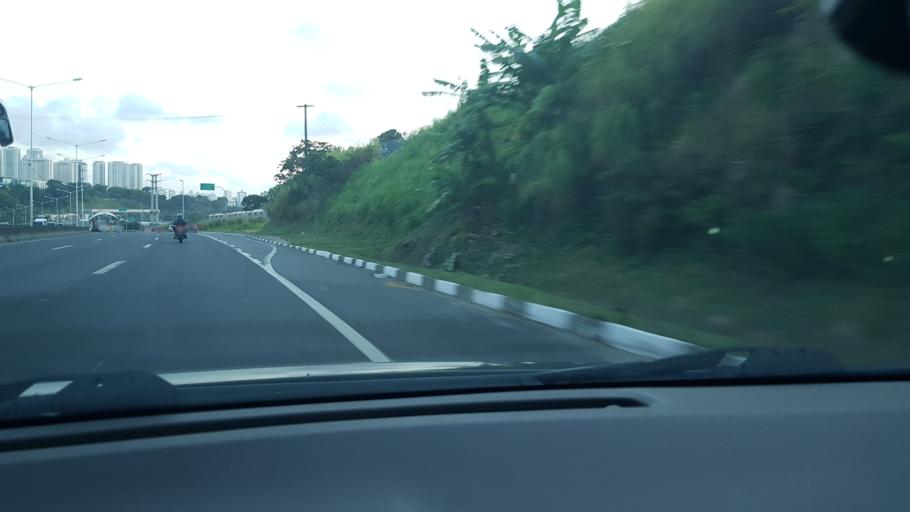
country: BR
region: Bahia
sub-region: Salvador
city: Salvador
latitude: -12.9504
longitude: -38.4707
